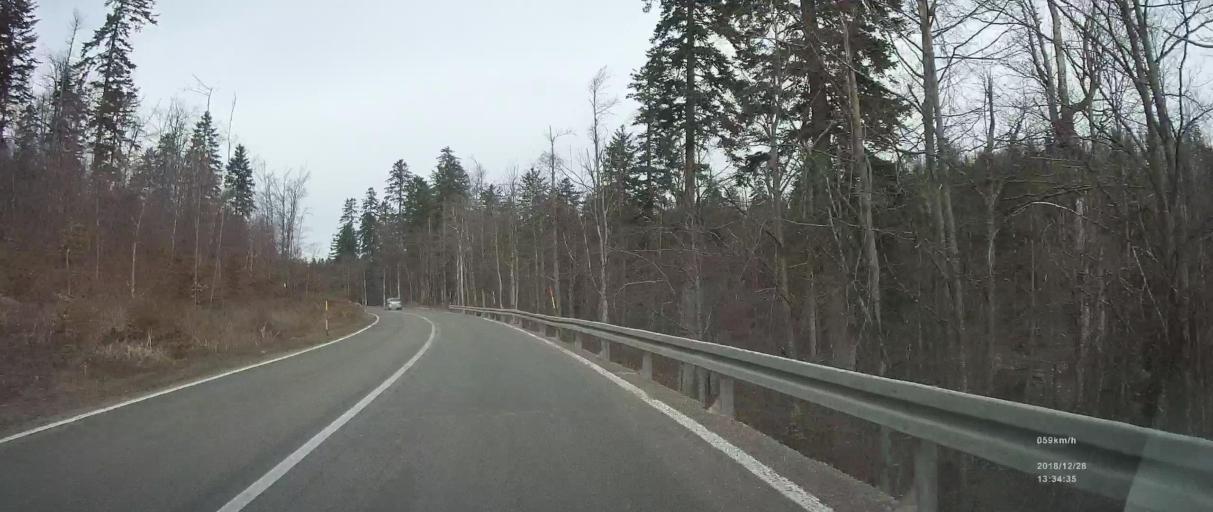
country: HR
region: Primorsko-Goranska
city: Hreljin
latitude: 45.3419
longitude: 14.6912
